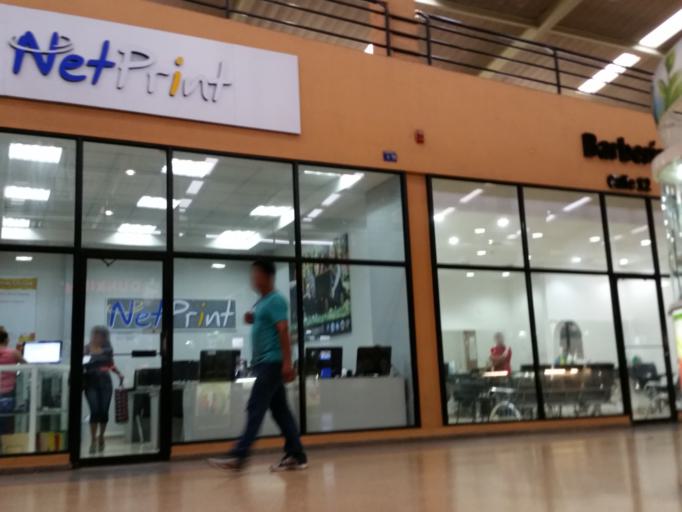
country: PA
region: Panama
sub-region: Distrito de Panama
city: Ancon
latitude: 8.9736
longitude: -79.5518
